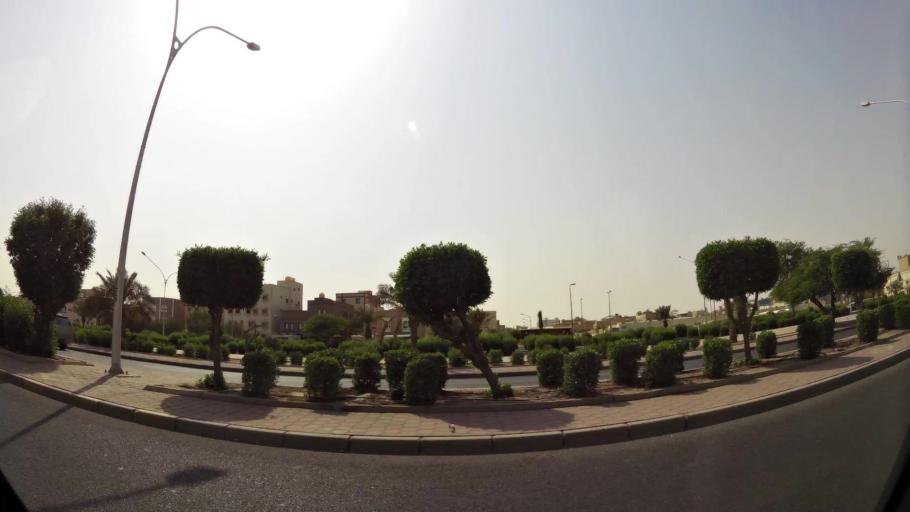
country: KW
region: Muhafazat al Jahra'
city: Al Jahra'
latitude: 29.3379
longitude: 47.6938
